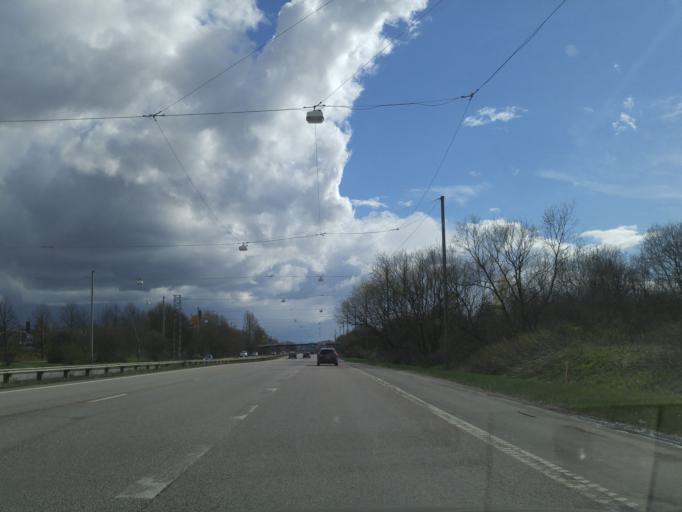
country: SE
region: Vaestra Goetaland
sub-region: Goteborg
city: Majorna
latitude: 57.6676
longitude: 11.9374
